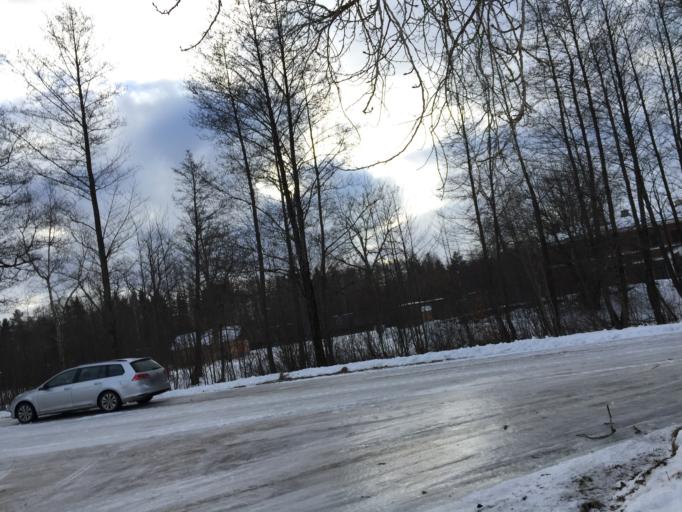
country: LV
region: Lielvarde
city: Lielvarde
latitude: 56.5765
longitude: 24.7938
